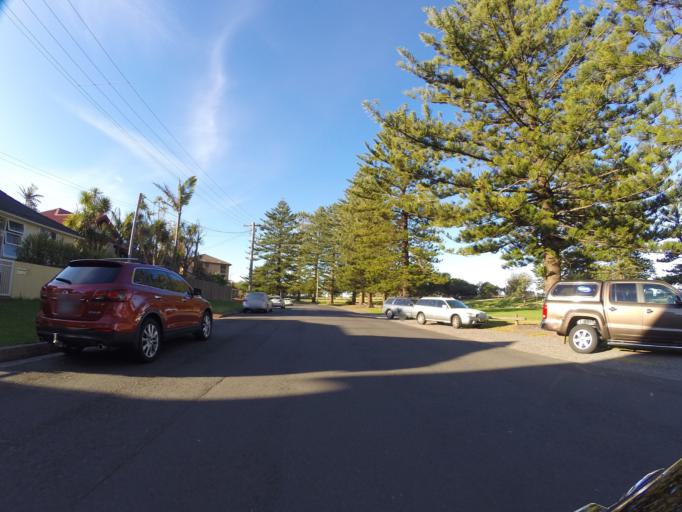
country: AU
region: New South Wales
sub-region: Wollongong
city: Bulli
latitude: -34.3155
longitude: 150.9271
